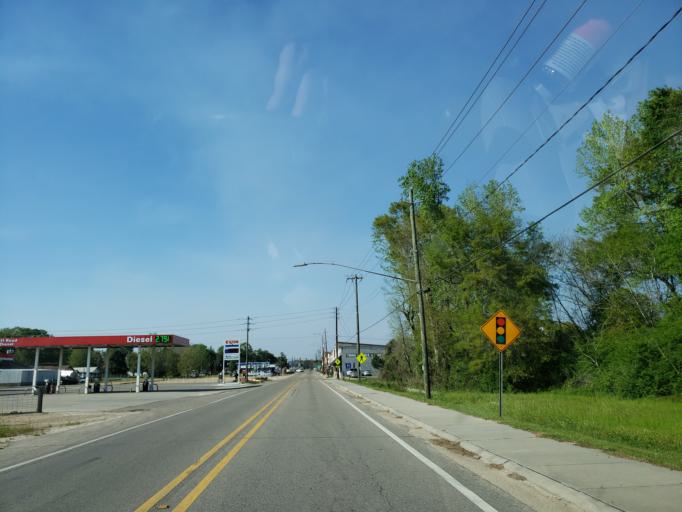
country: US
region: Mississippi
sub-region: Perry County
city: Richton
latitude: 31.3460
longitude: -88.9361
